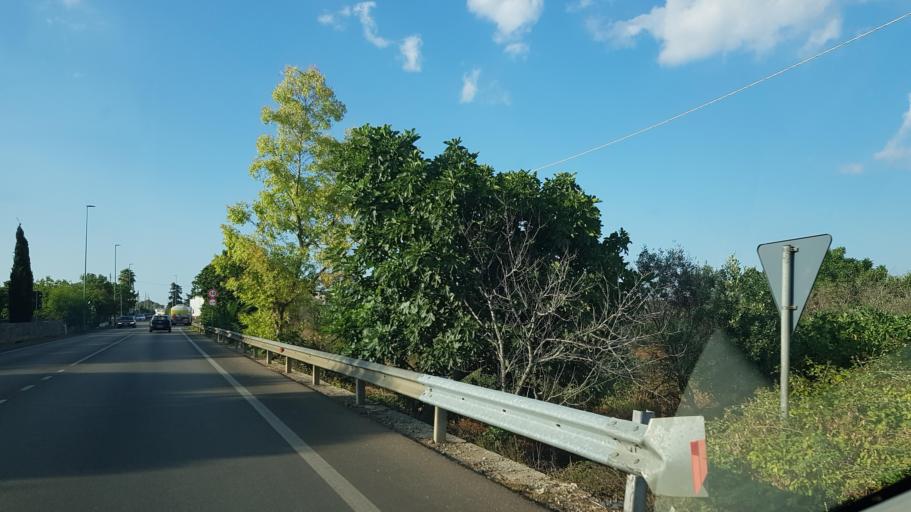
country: IT
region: Apulia
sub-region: Provincia di Lecce
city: Montesano Salentino
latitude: 39.9668
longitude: 18.3231
